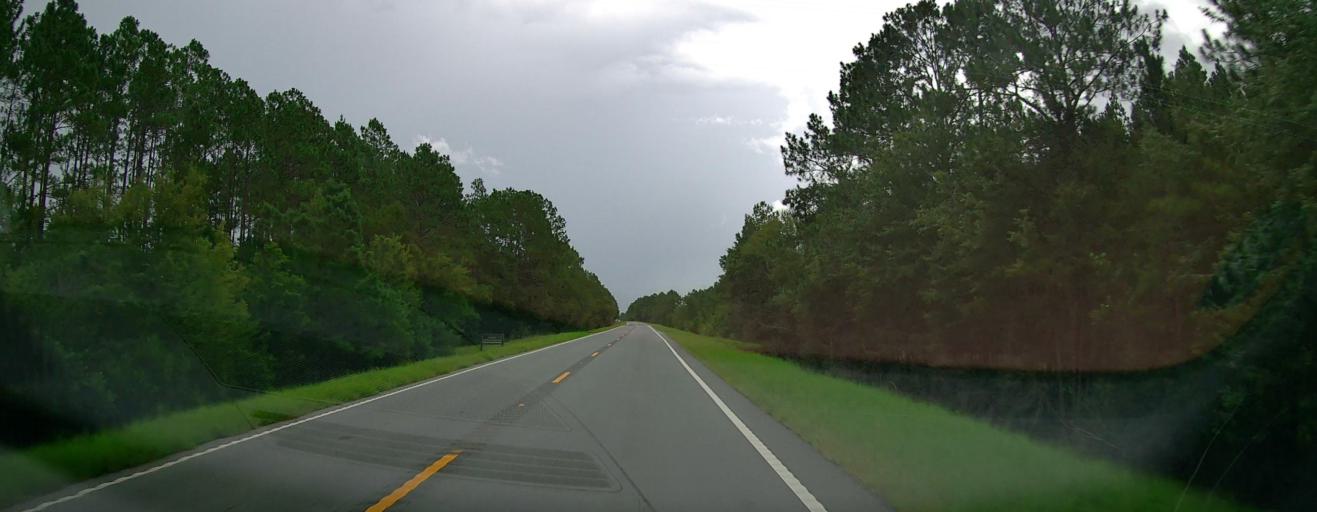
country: US
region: Georgia
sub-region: Brantley County
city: Nahunta
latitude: 31.3497
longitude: -82.0273
